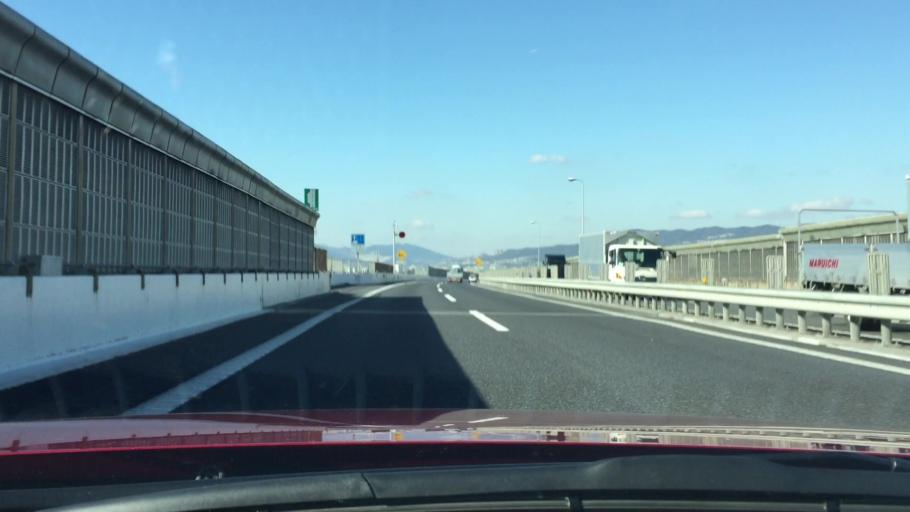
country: JP
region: Osaka
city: Ikeda
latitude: 34.8016
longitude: 135.4404
